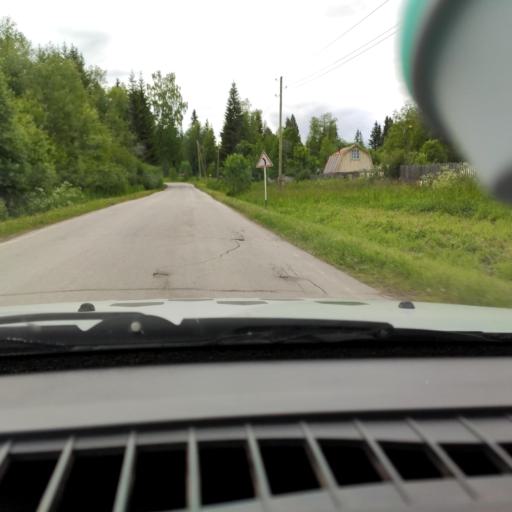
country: RU
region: Perm
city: Lys'va
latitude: 58.1178
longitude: 57.6959
